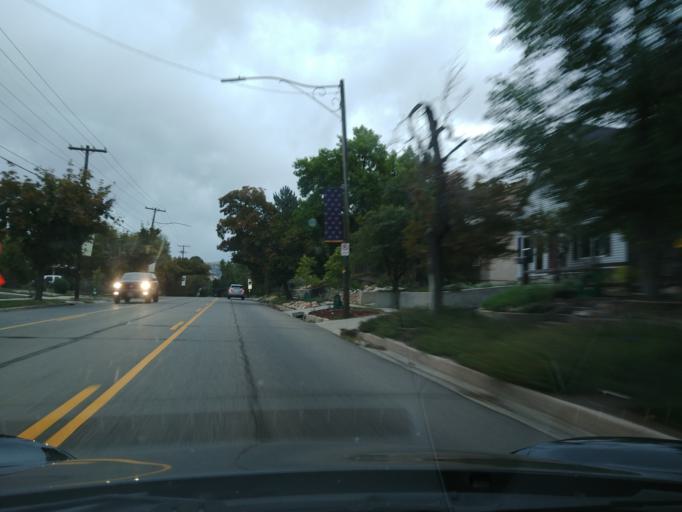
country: US
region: Utah
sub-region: Salt Lake County
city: Willard
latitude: 40.7284
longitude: -111.8539
